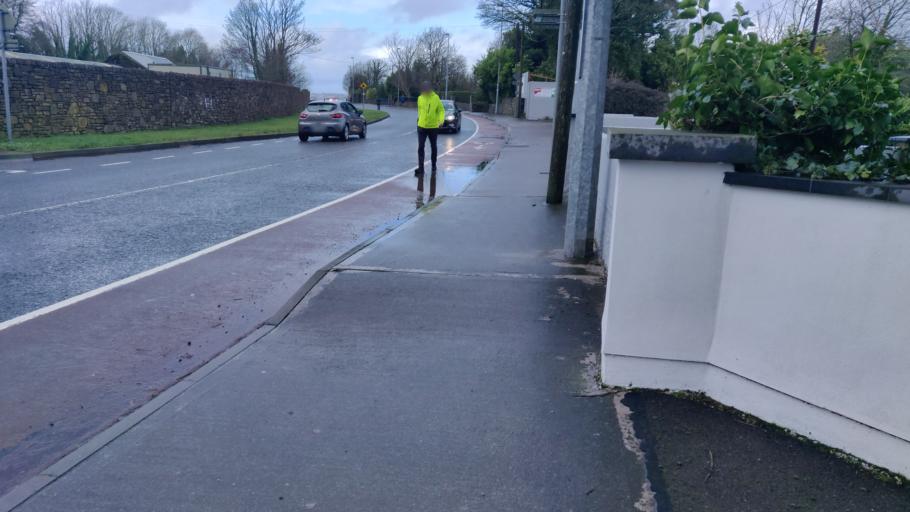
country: IE
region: Munster
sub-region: County Cork
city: Cork
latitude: 51.8697
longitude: -8.4175
